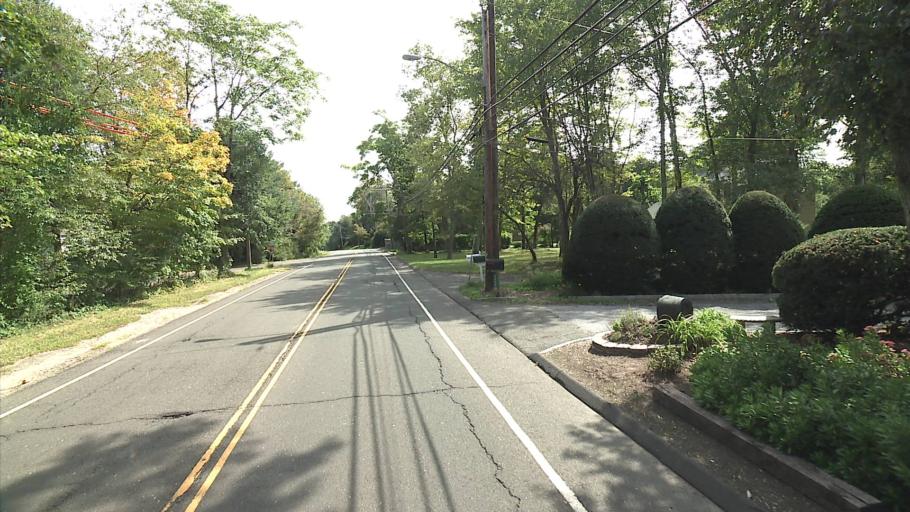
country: US
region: Connecticut
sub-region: Fairfield County
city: North Stamford
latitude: 41.1493
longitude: -73.5522
